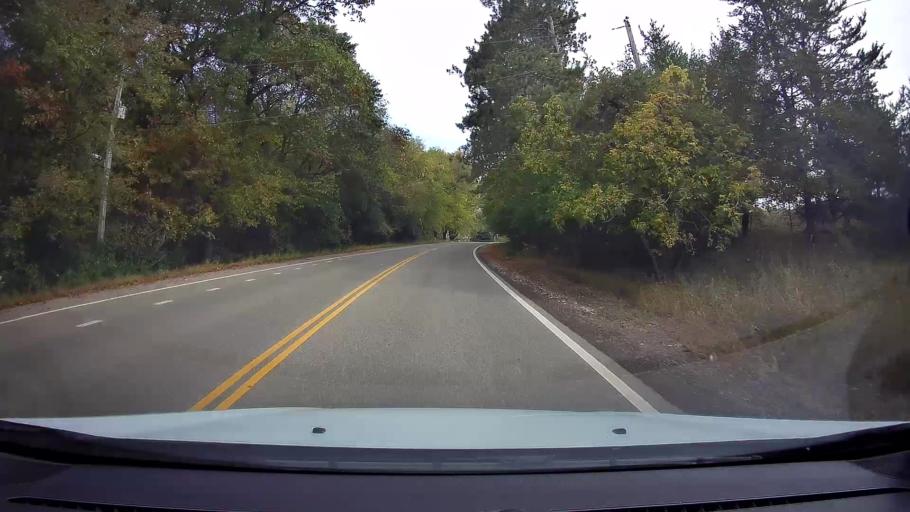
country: US
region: Minnesota
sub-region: Washington County
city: Stillwater
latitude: 45.0944
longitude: -92.8223
